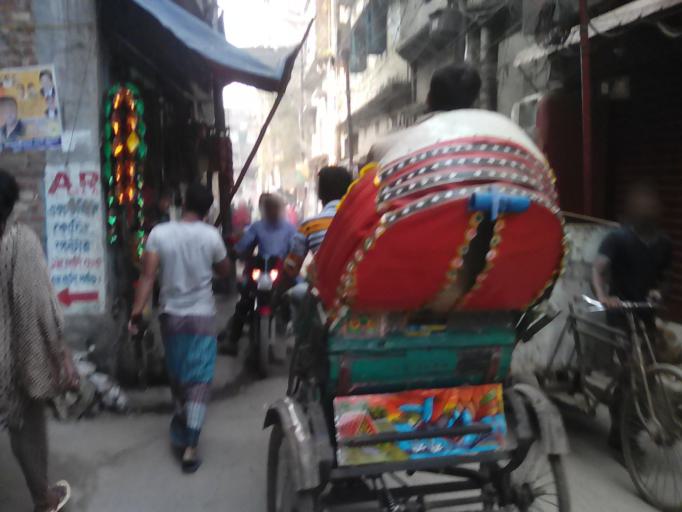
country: BD
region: Dhaka
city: Azimpur
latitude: 23.7223
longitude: 90.3783
